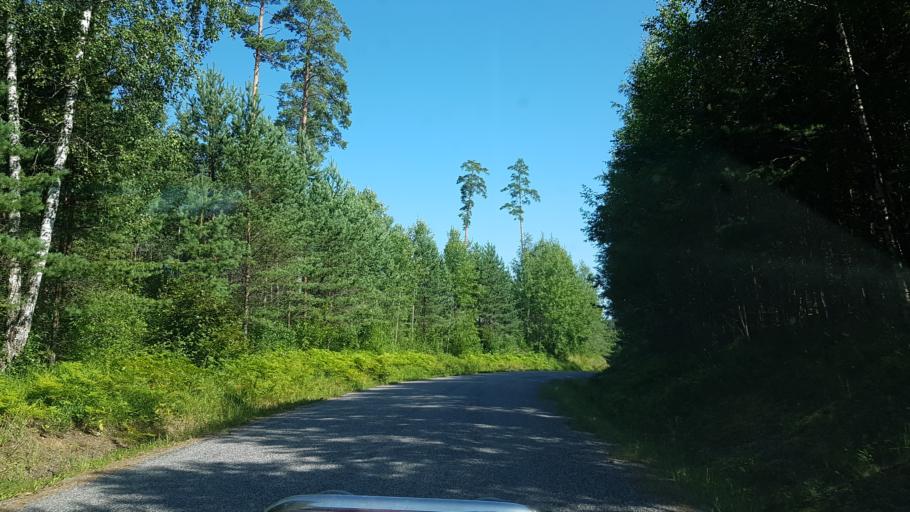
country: EE
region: Vorumaa
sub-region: Voru linn
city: Voru
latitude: 57.7163
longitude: 27.1975
